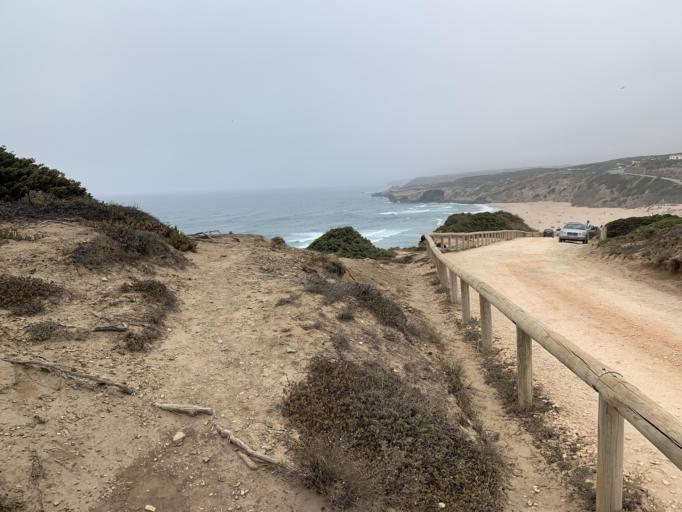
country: PT
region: Faro
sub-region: Aljezur
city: Aljezur
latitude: 37.3393
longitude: -8.8561
